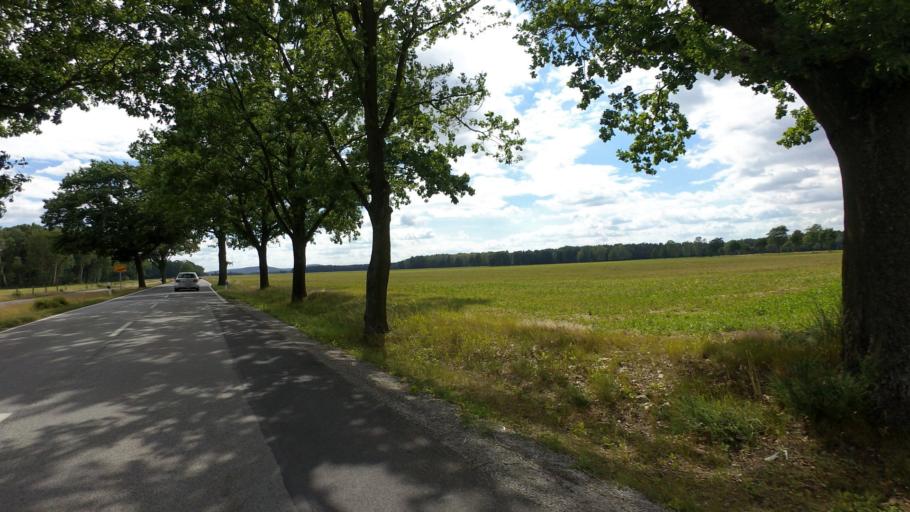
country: DE
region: Saxony
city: Ossling
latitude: 51.3271
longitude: 14.1524
